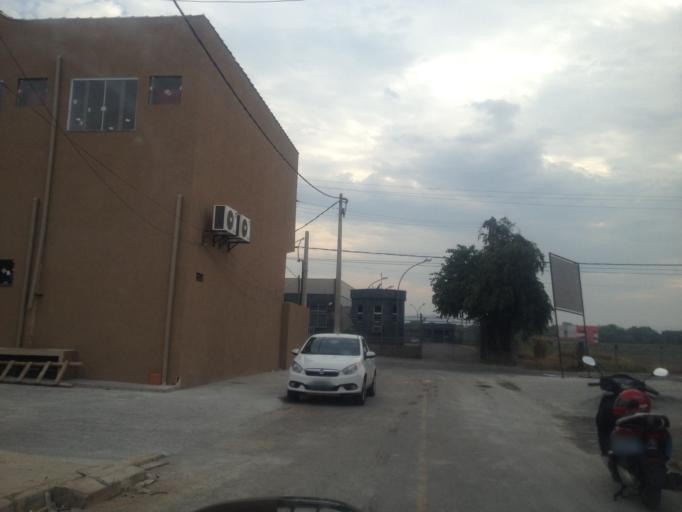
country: BR
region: Rio de Janeiro
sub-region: Porto Real
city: Porto Real
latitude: -22.4202
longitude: -44.3024
